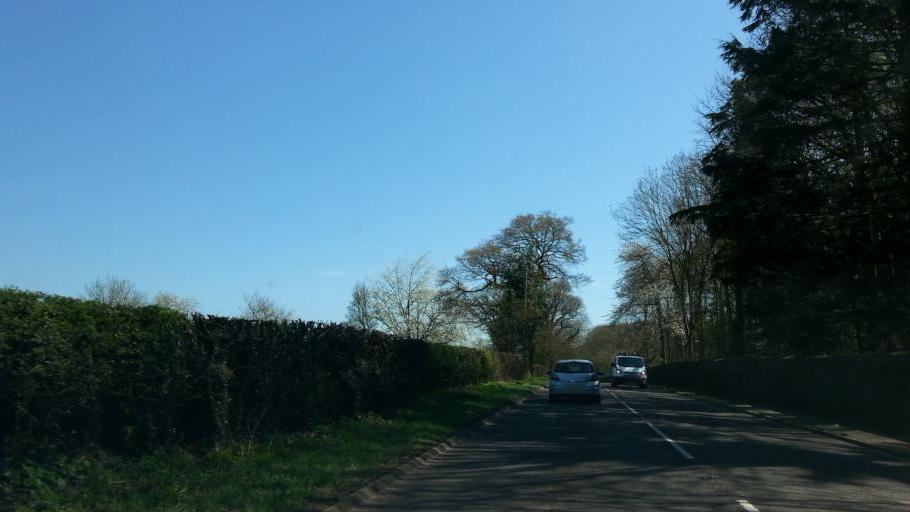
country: GB
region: England
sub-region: Shropshire
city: Tong
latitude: 52.6948
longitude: -2.2742
